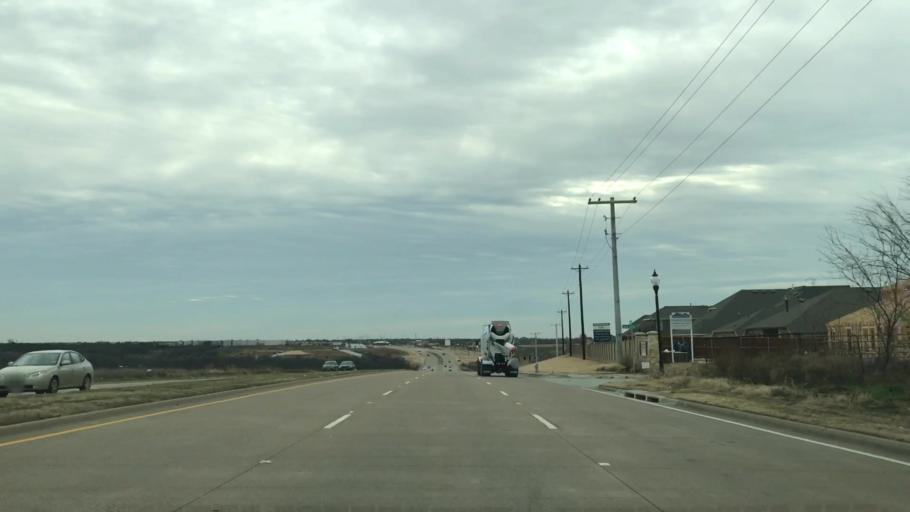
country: US
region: Texas
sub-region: Denton County
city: The Colony
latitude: 33.0570
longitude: -96.8852
